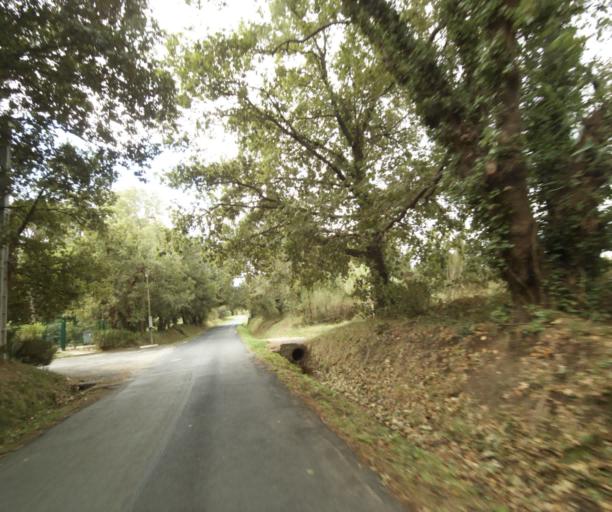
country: FR
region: Languedoc-Roussillon
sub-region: Departement des Pyrenees-Orientales
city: Argelers
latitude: 42.5588
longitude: 3.0269
